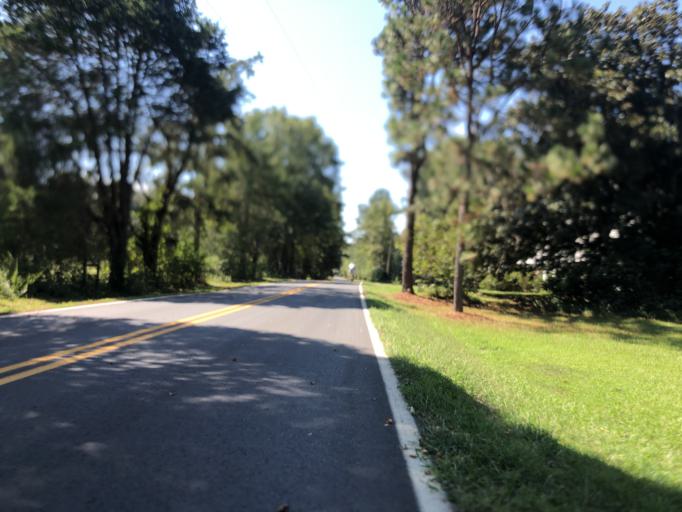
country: US
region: Georgia
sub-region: Heard County
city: Franklin
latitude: 33.3821
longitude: -84.9686
